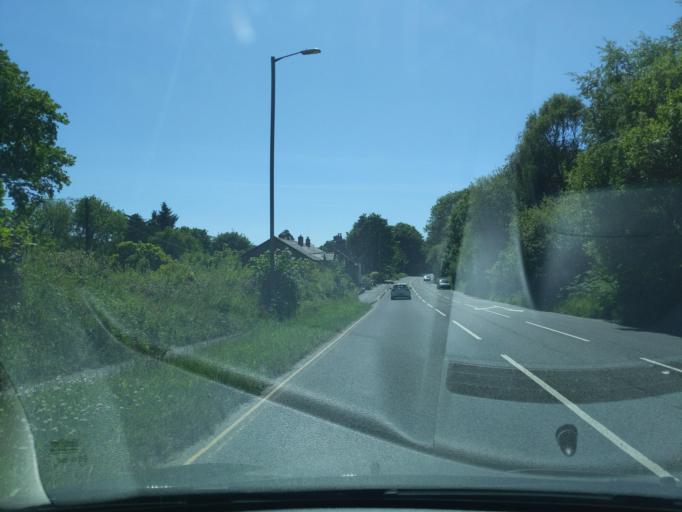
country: GB
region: England
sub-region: Cornwall
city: Par
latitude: 50.3478
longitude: -4.7355
